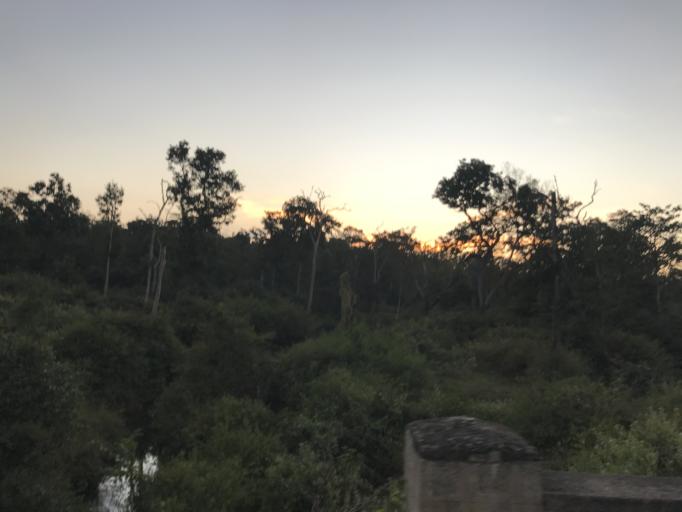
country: IN
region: Karnataka
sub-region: Mysore
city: Heggadadevankote
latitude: 11.9763
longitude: 76.2403
